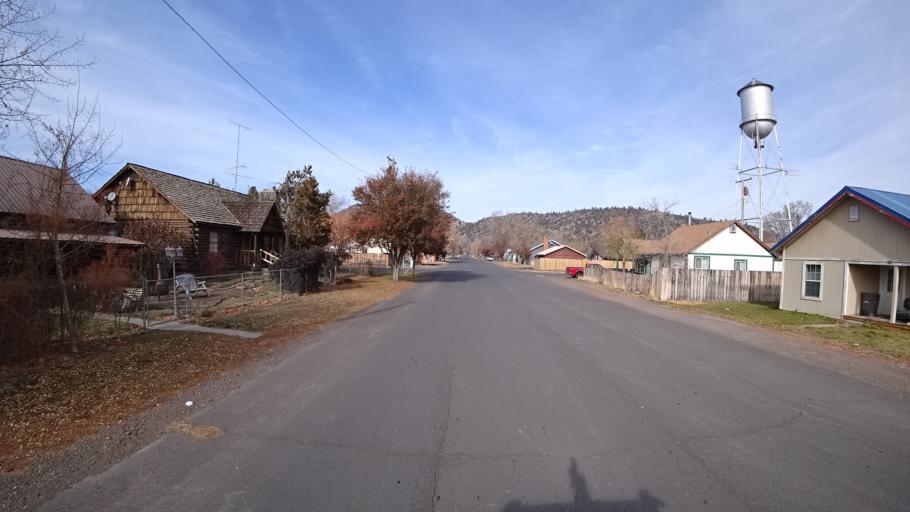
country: US
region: Oregon
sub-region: Klamath County
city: Klamath Falls
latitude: 41.9653
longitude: -121.9207
